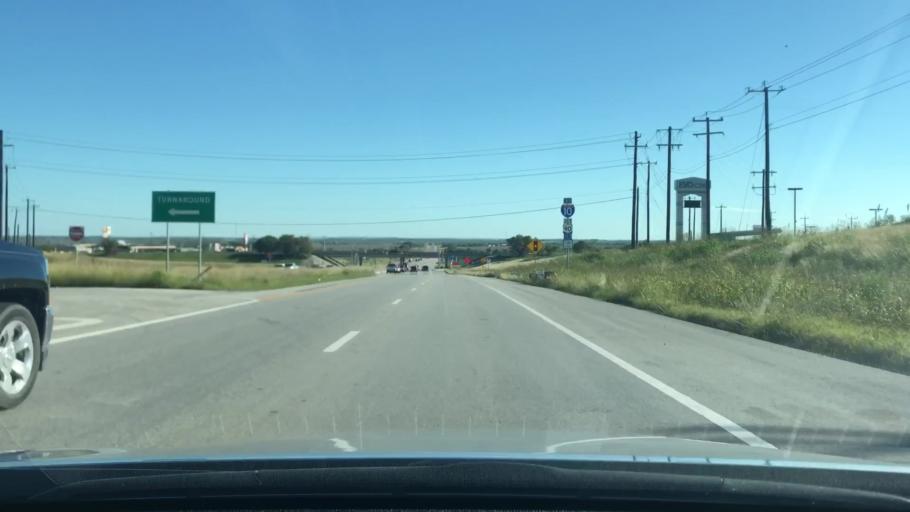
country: US
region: Texas
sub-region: Bexar County
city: Converse
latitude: 29.4686
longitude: -98.2935
